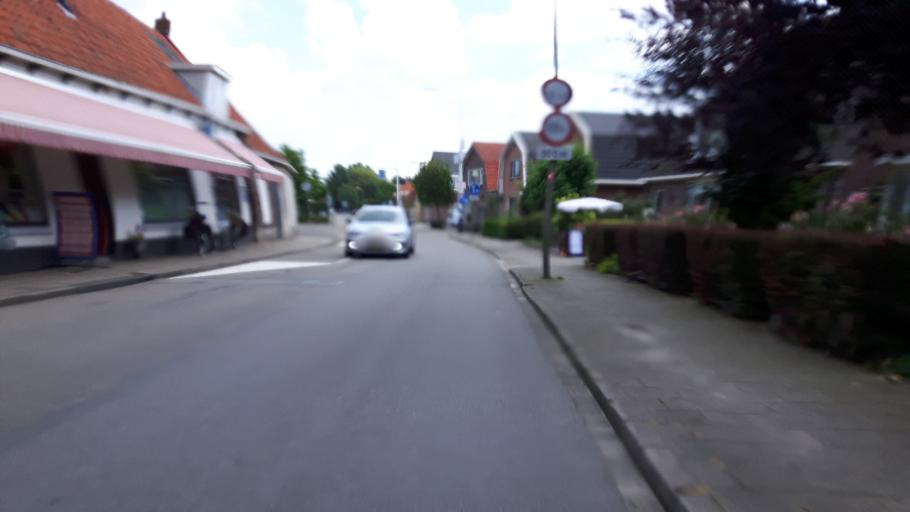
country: NL
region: South Holland
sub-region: Bodegraven-Reeuwijk
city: Bodegraven
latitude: 52.0776
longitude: 4.8122
